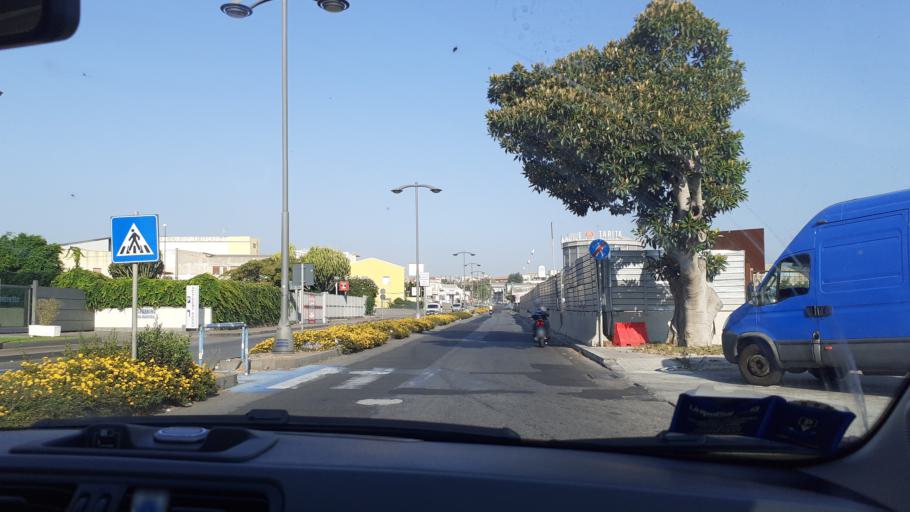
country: IT
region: Sicily
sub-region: Catania
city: Misterbianco
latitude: 37.5137
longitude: 15.0269
